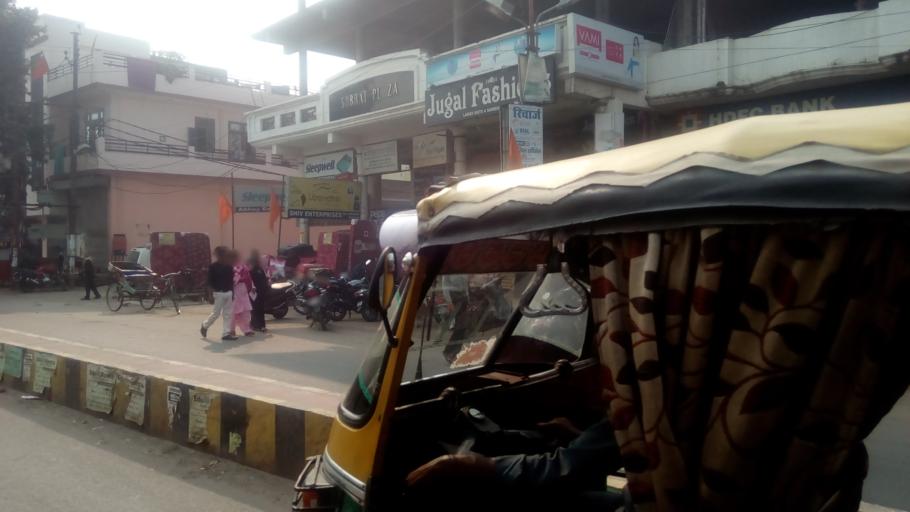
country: IN
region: Uttar Pradesh
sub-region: Lucknow District
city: Lucknow
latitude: 26.8454
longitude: 80.8775
